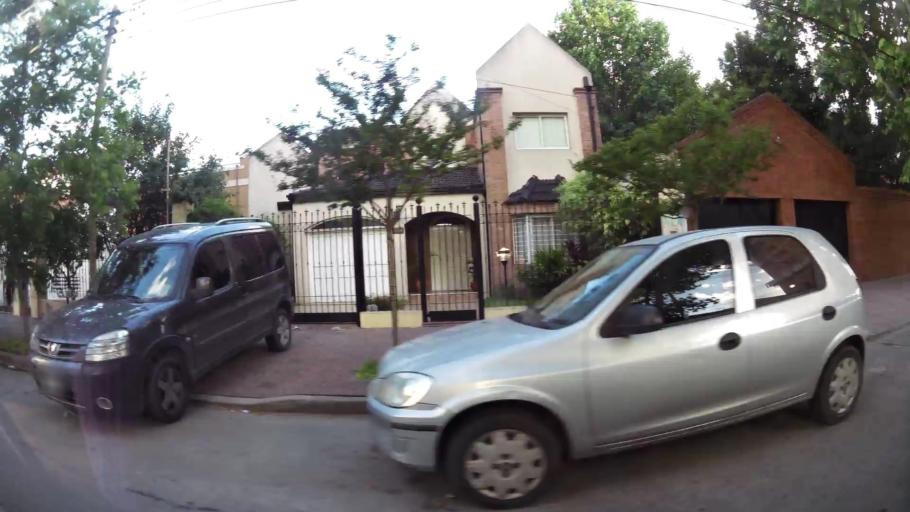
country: AR
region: Buenos Aires
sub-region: Partido de General San Martin
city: General San Martin
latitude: -34.5506
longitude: -58.5501
